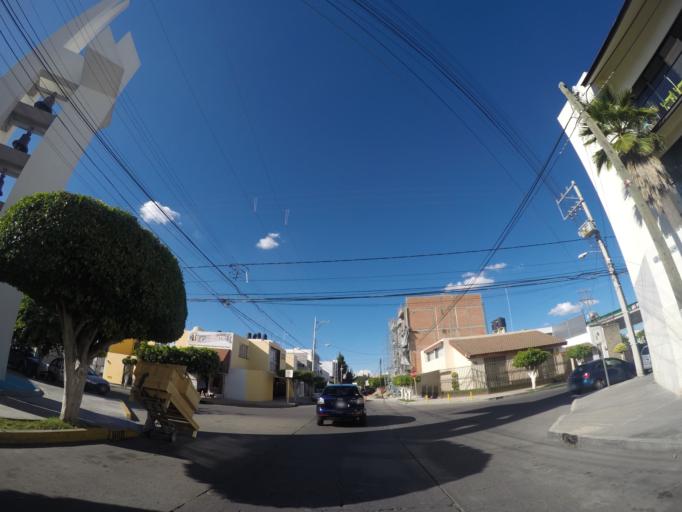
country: MX
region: San Luis Potosi
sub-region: San Luis Potosi
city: San Luis Potosi
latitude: 22.1452
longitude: -101.0028
